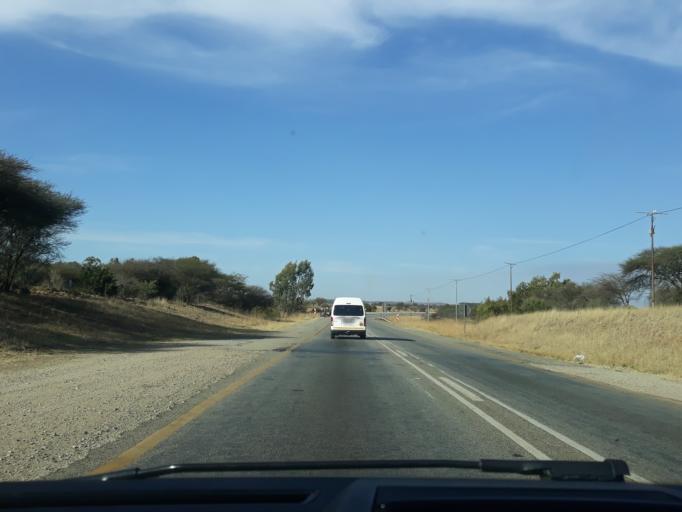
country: ZA
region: Limpopo
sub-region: Capricorn District Municipality
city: Polokwane
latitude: -23.9498
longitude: 29.4014
